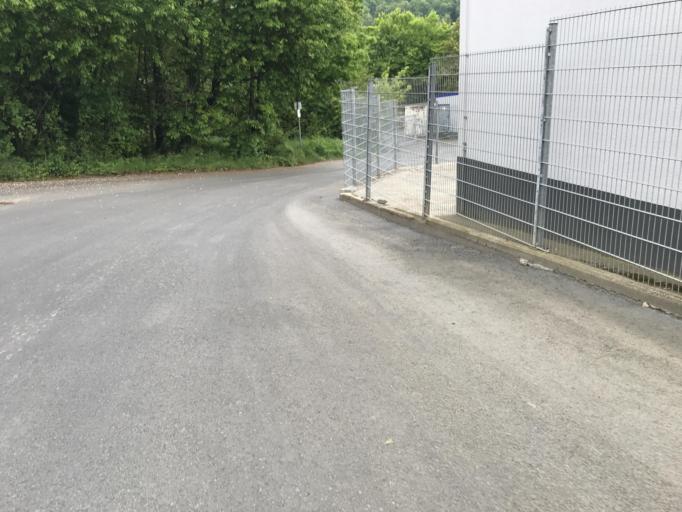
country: DE
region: Hesse
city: Budingen
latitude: 50.3010
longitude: 9.1050
